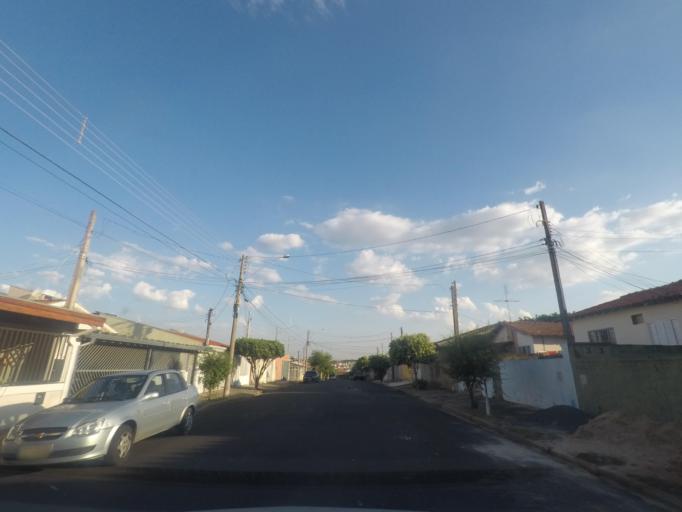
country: BR
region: Sao Paulo
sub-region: Sumare
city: Sumare
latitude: -22.8131
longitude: -47.2839
